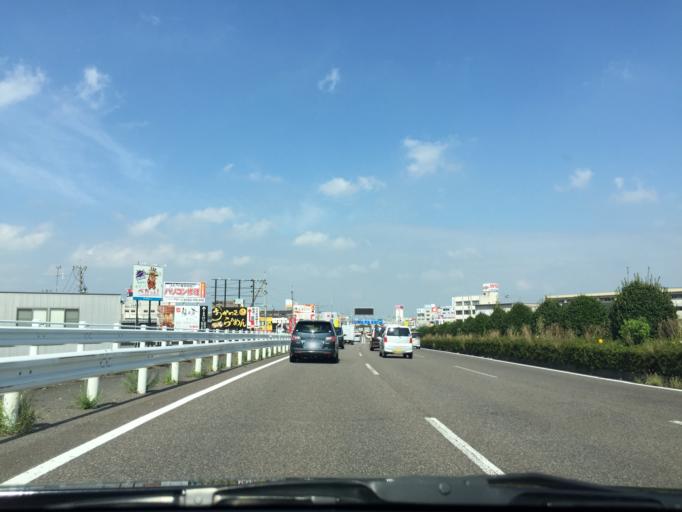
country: JP
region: Gifu
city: Kasamatsucho
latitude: 35.3897
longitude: 136.7408
